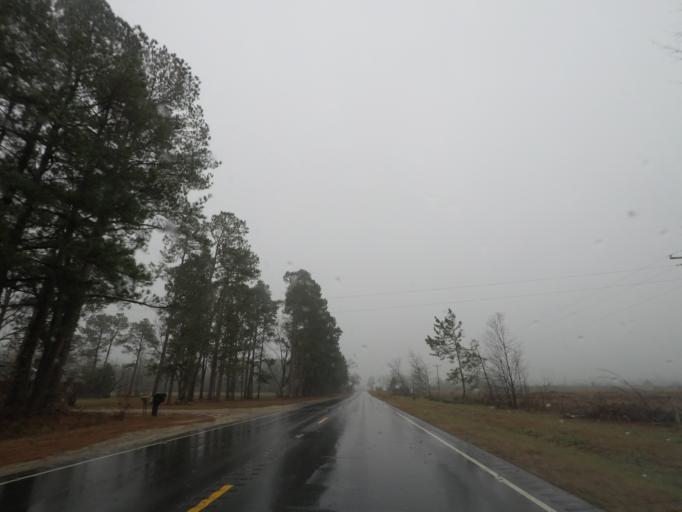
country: US
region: North Carolina
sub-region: Scotland County
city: Laurinburg
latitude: 34.8457
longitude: -79.4587
